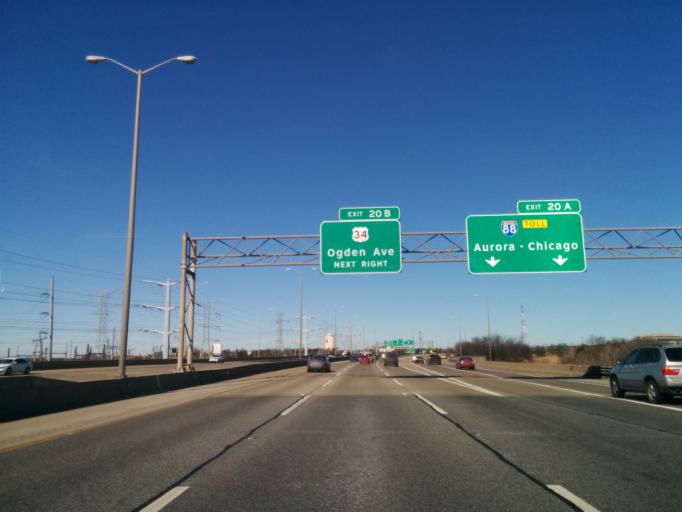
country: US
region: Illinois
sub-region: DuPage County
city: Lisle
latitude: 41.7956
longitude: -88.0567
